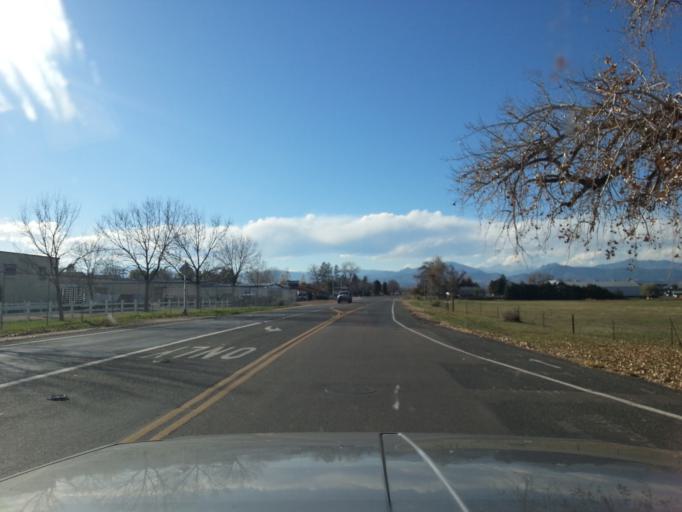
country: US
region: Colorado
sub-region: Larimer County
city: Loveland
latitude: 40.3923
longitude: -105.1065
